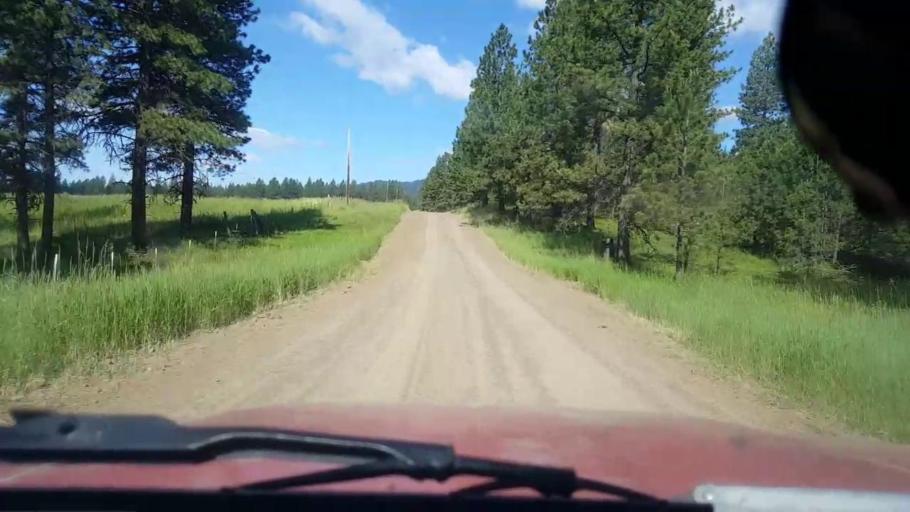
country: US
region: Washington
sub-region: Garfield County
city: Pomeroy
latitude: 46.0370
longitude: -117.4205
